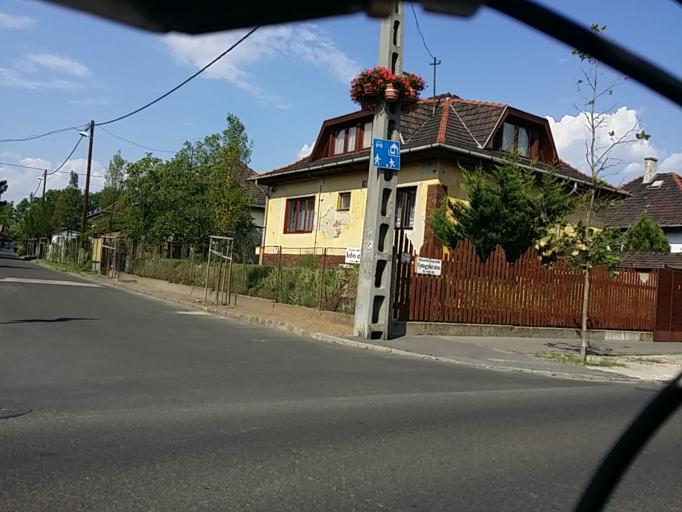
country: HU
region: Budapest
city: Budapest IV. keruelet
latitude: 47.5465
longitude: 19.0882
